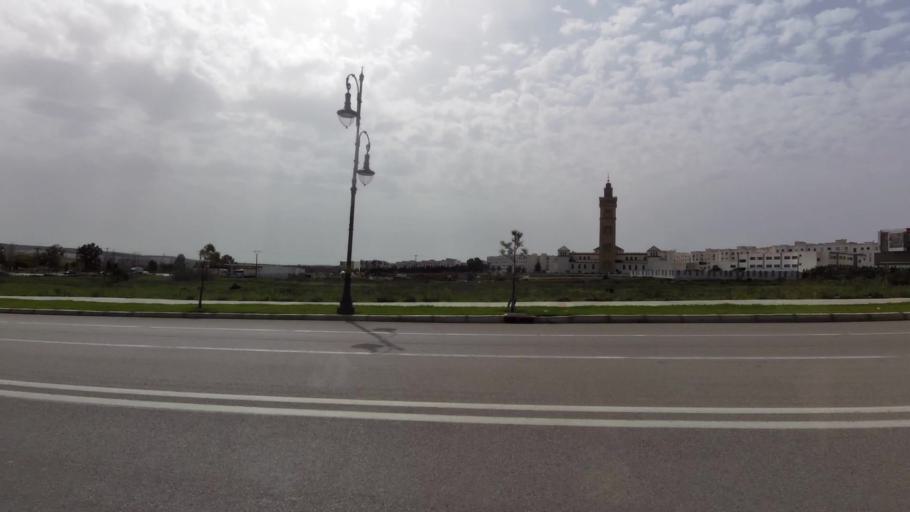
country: MA
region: Tanger-Tetouan
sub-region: Tanger-Assilah
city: Boukhalef
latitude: 35.7327
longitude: -5.8740
